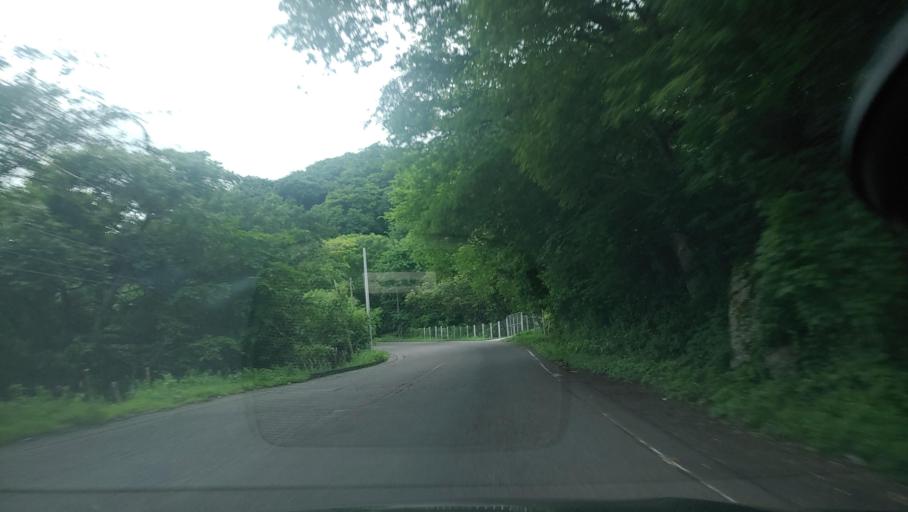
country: HN
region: Choluteca
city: Corpus
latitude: 13.3747
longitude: -87.0489
